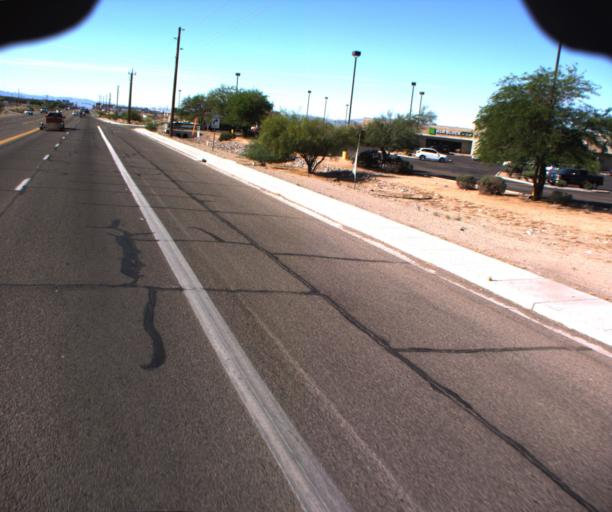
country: US
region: Arizona
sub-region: Mohave County
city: Mohave Valley
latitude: 35.0177
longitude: -114.5981
